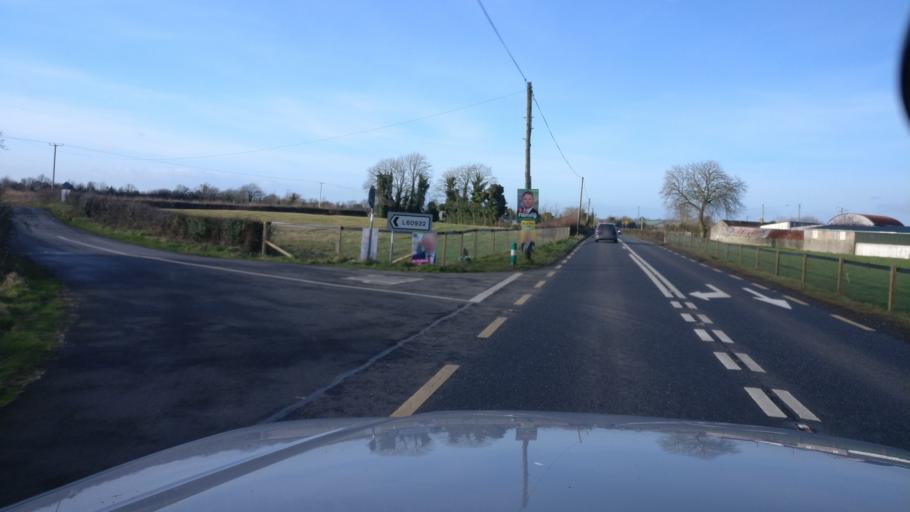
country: IE
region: Leinster
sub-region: Laois
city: Mountmellick
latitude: 53.1699
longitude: -7.3798
